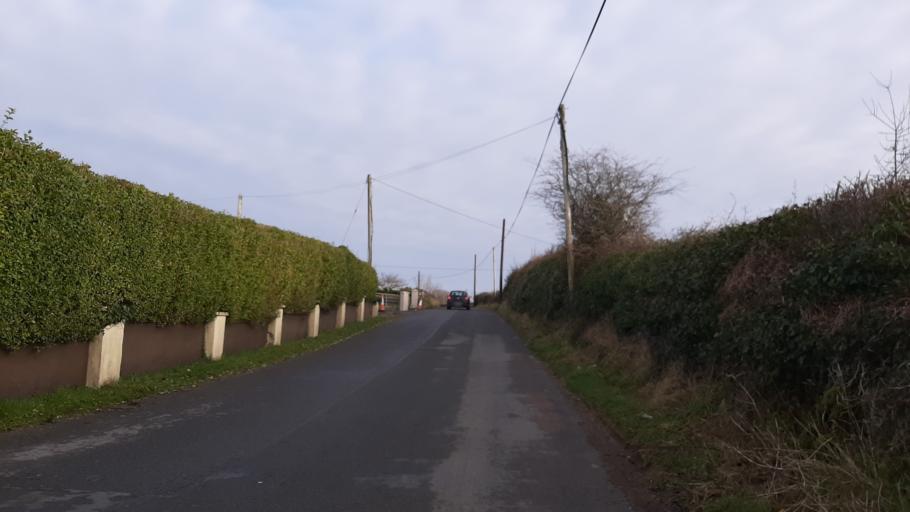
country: IE
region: Connaught
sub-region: County Galway
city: Gaillimh
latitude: 53.3064
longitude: -9.0606
